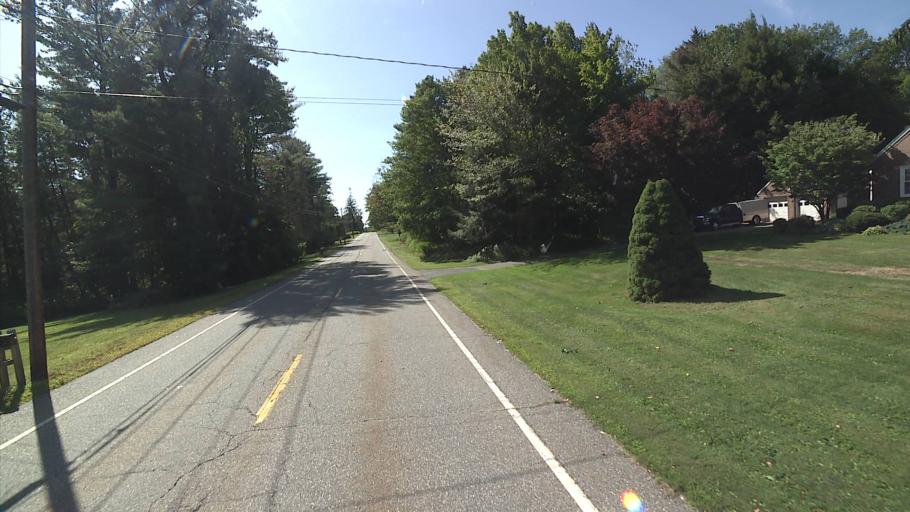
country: US
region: Connecticut
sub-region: Litchfield County
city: Northwest Harwinton
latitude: 41.7593
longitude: -73.0837
